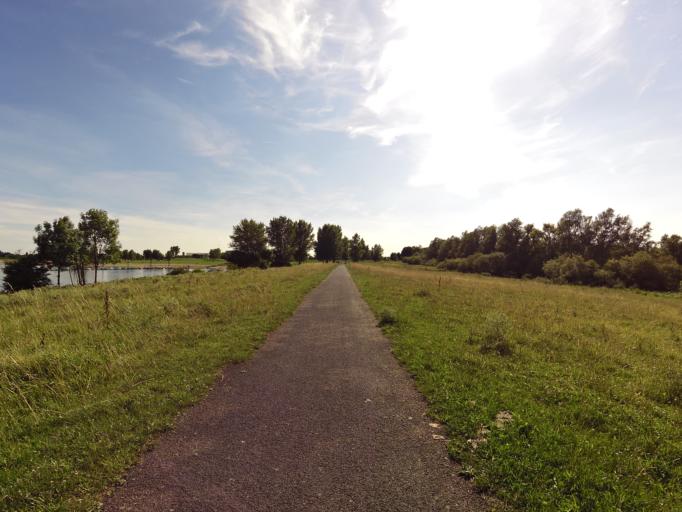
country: NL
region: Gelderland
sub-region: Gemeente Zevenaar
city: Zevenaar
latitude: 51.8716
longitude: 6.0814
